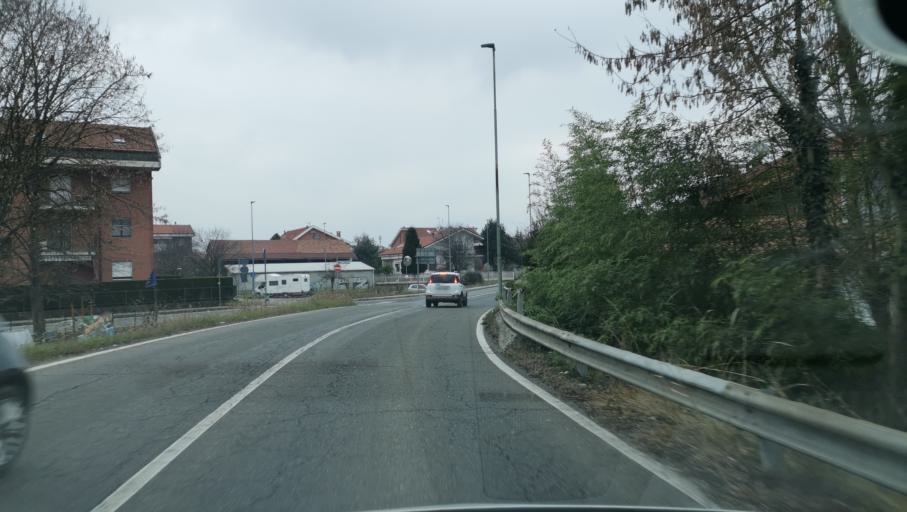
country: IT
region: Piedmont
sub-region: Provincia di Torino
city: Settimo Torinese
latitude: 45.1332
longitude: 7.7795
